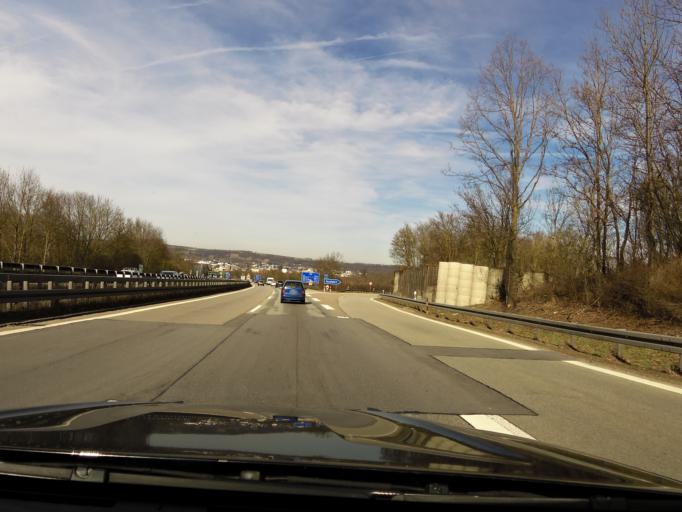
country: DE
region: Bavaria
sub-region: Upper Palatinate
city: Pentling
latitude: 48.9996
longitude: 12.0636
